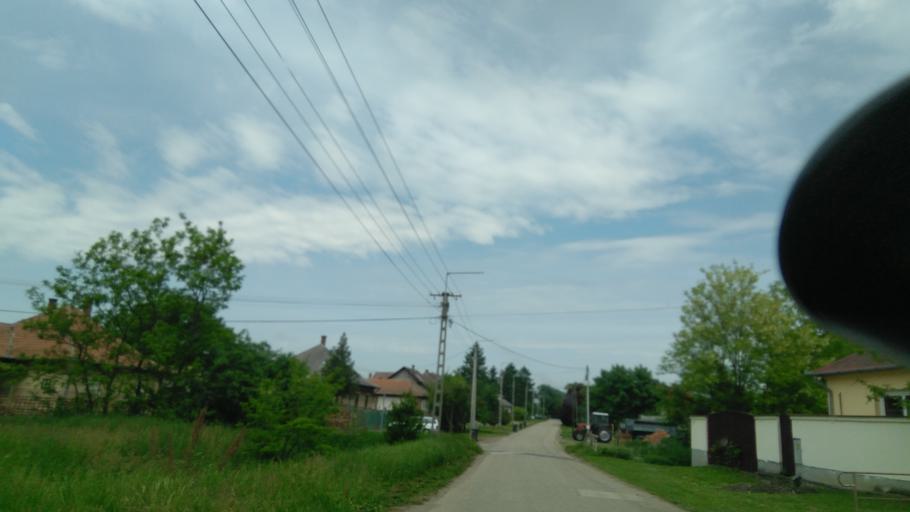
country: HU
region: Bekes
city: Fuzesgyarmat
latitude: 47.1037
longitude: 21.2055
